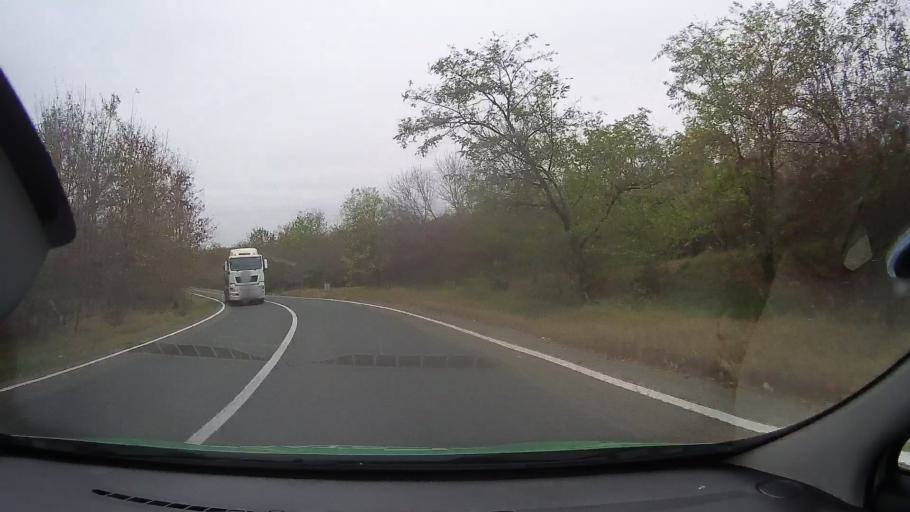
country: RO
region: Constanta
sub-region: Comuna Garliciu
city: Garliciu
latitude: 44.7105
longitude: 28.0771
